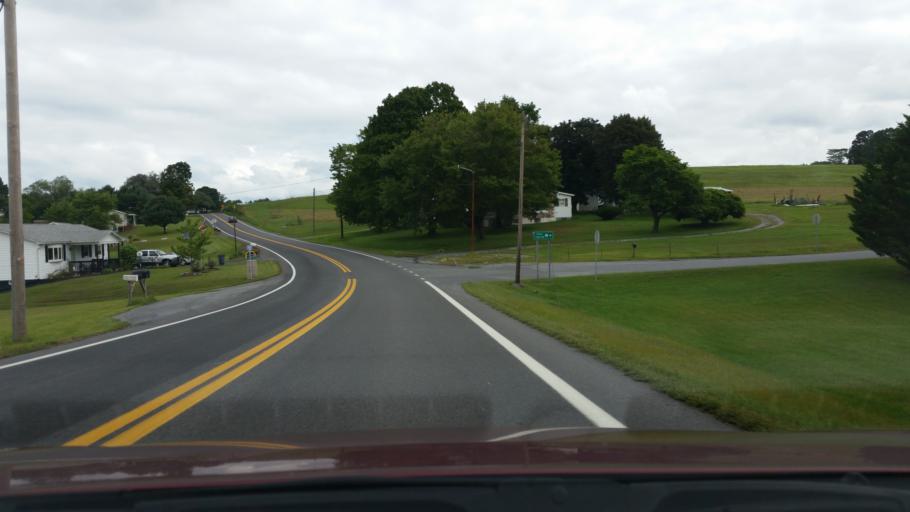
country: US
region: West Virginia
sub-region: Morgan County
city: Berkeley Springs
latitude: 39.6240
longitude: -78.1905
